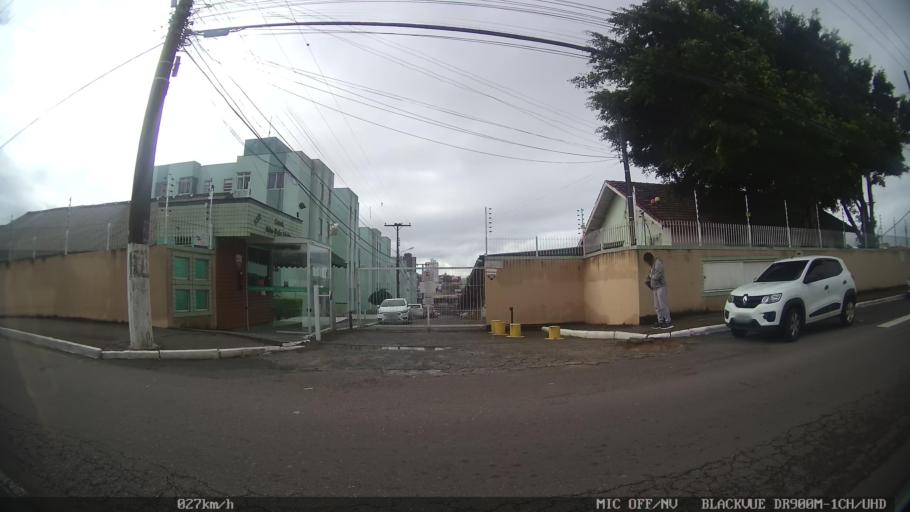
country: BR
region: Santa Catarina
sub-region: Sao Jose
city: Campinas
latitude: -27.5771
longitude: -48.6237
